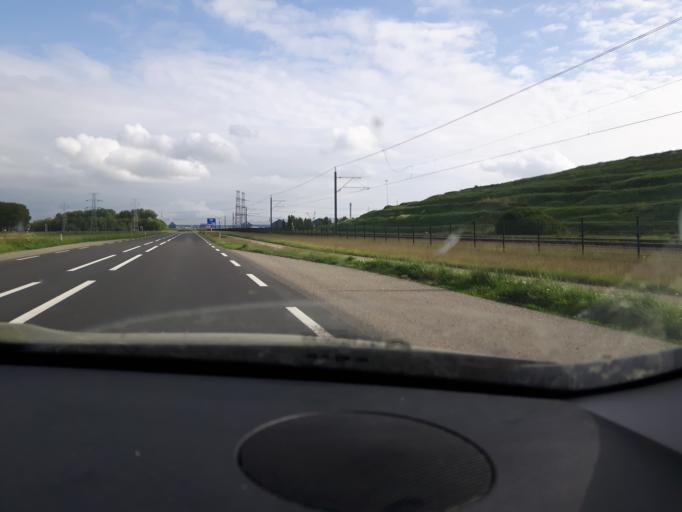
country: NL
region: Zeeland
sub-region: Gemeente Borsele
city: Borssele
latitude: 51.4678
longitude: 3.7263
